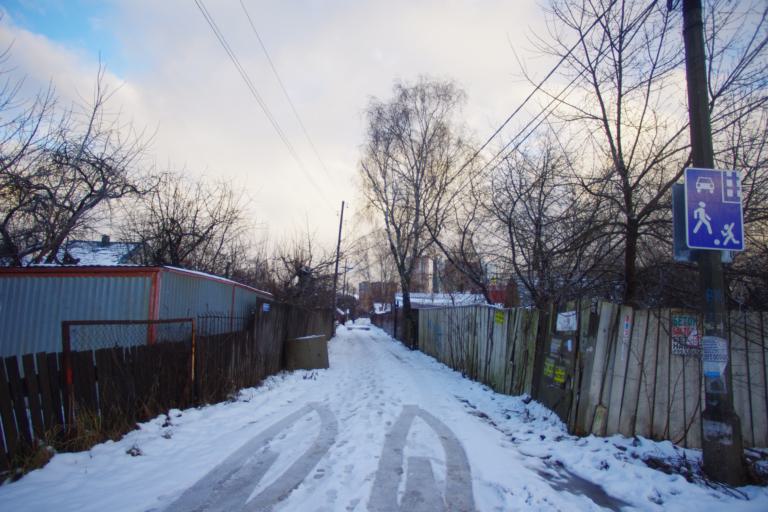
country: RU
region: Moskovskaya
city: Pavshino
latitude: 55.8105
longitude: 37.3431
